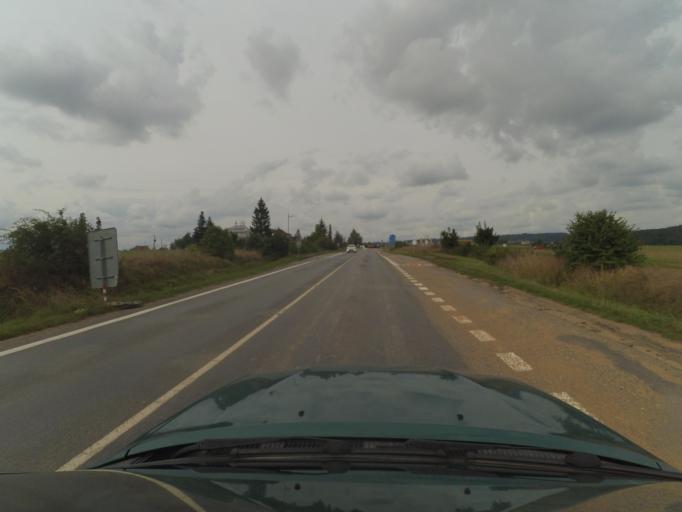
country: CZ
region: Central Bohemia
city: Luzna
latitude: 50.1708
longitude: 13.7409
